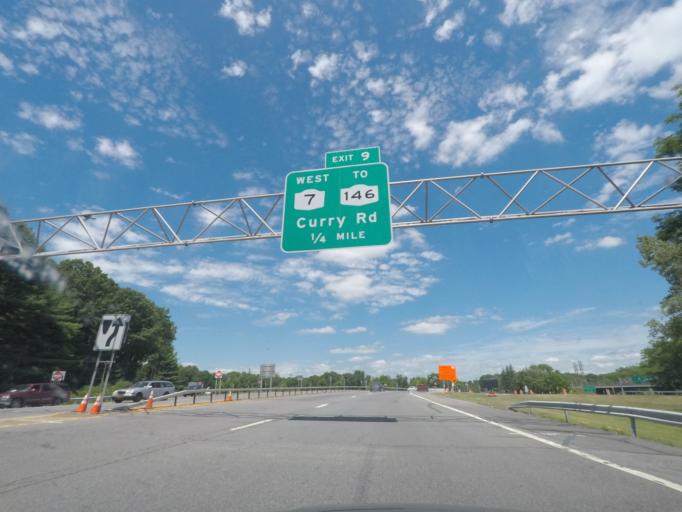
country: US
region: New York
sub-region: Schenectady County
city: Rotterdam
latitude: 42.7578
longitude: -73.9329
